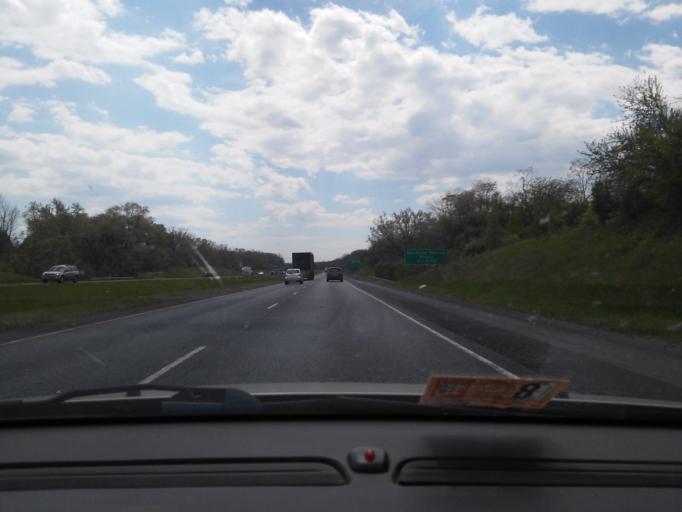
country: US
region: Virginia
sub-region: City of Winchester
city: Winchester
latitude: 39.1791
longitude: -78.1435
